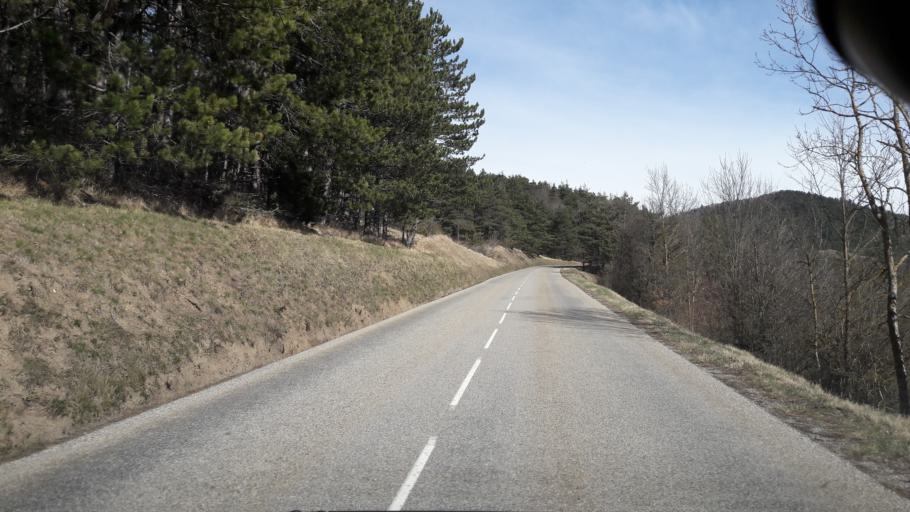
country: FR
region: Rhone-Alpes
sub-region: Departement de l'Isere
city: Mens
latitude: 44.8346
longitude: 5.7737
